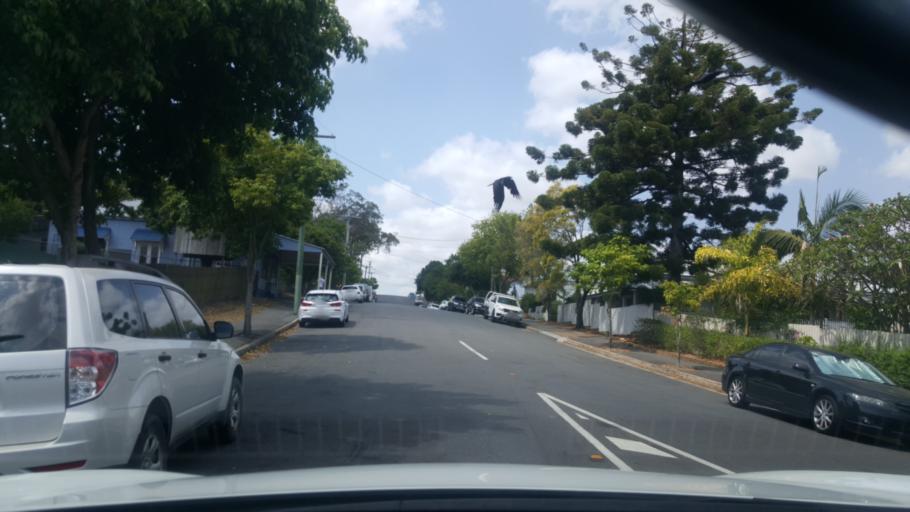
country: AU
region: Queensland
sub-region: Brisbane
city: South Brisbane
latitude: -27.4854
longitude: 153.0228
